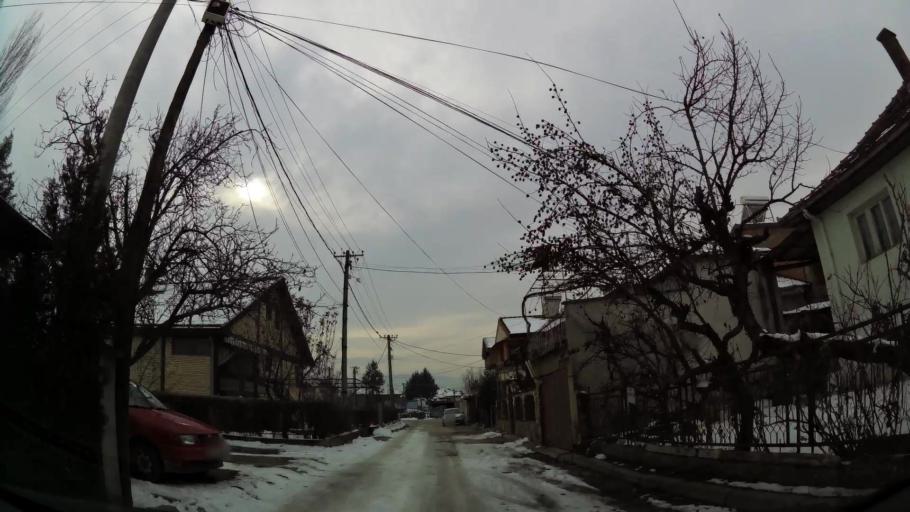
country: MK
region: Butel
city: Butel
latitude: 42.0374
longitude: 21.4523
